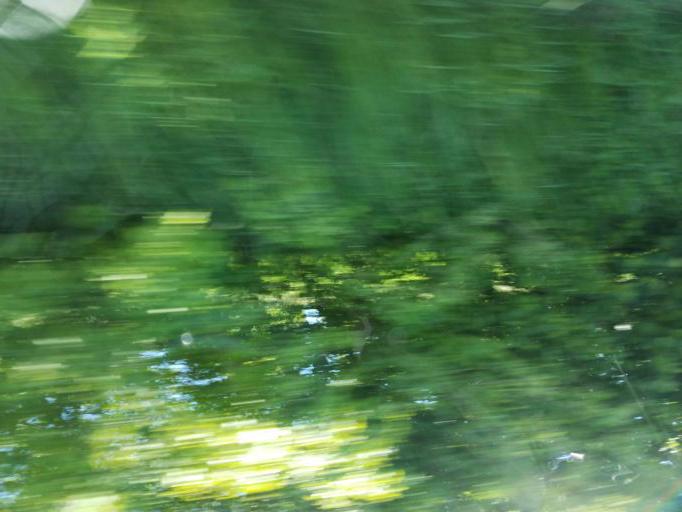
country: DE
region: Bavaria
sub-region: Upper Bavaria
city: Pocking
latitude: 47.9827
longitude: 11.3191
